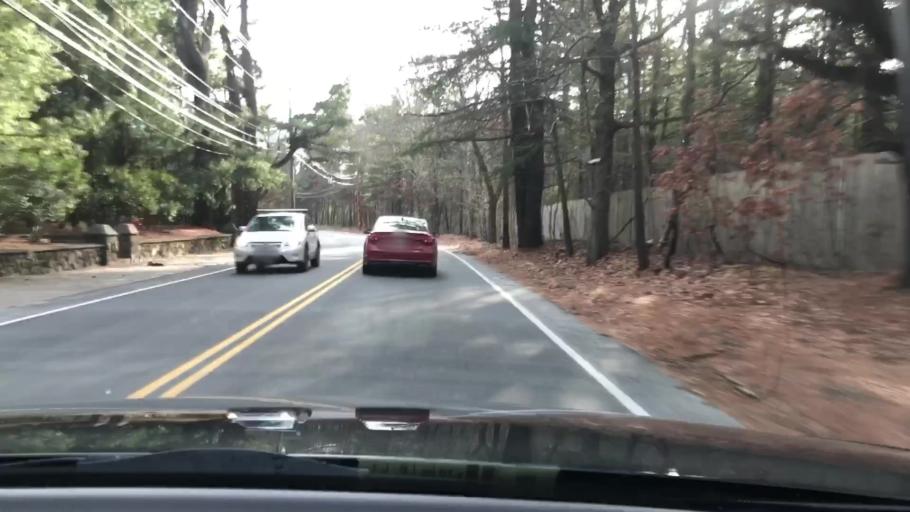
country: US
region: Massachusetts
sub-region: Worcester County
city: Milford
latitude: 42.1086
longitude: -71.5142
